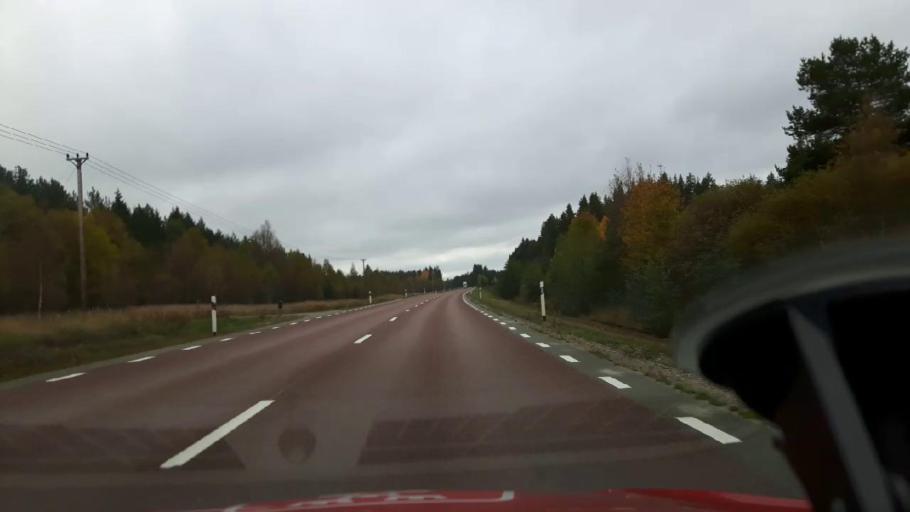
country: SE
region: Jaemtland
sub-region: Harjedalens Kommun
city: Sveg
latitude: 62.2549
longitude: 14.8207
